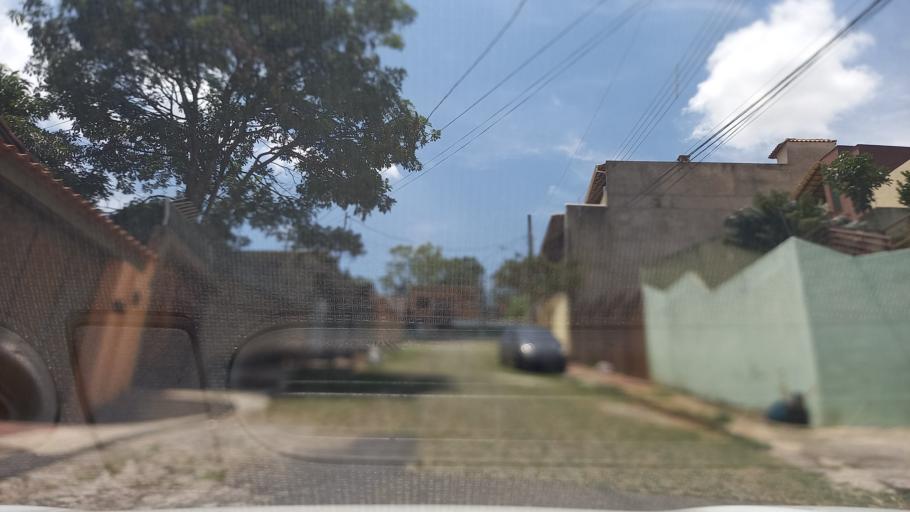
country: BR
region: Minas Gerais
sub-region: Contagem
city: Contagem
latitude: -19.9070
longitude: -44.0113
